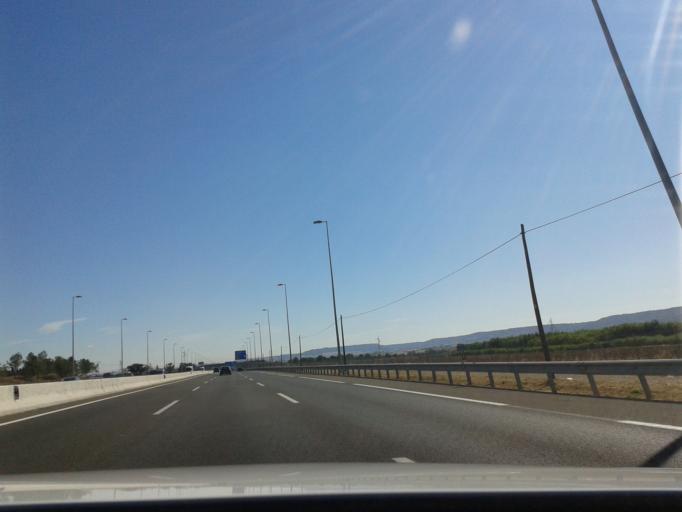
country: ES
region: Madrid
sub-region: Provincia de Madrid
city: Meco
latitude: 40.5202
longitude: -3.3065
